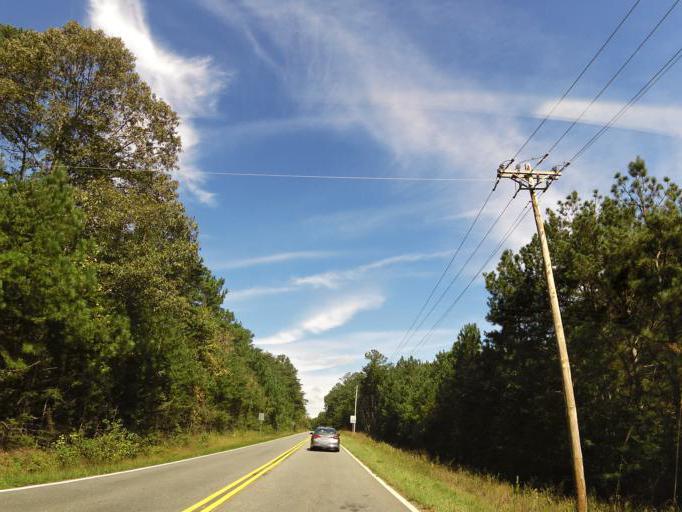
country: US
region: Georgia
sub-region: Pickens County
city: Nelson
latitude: 34.4283
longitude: -84.2758
